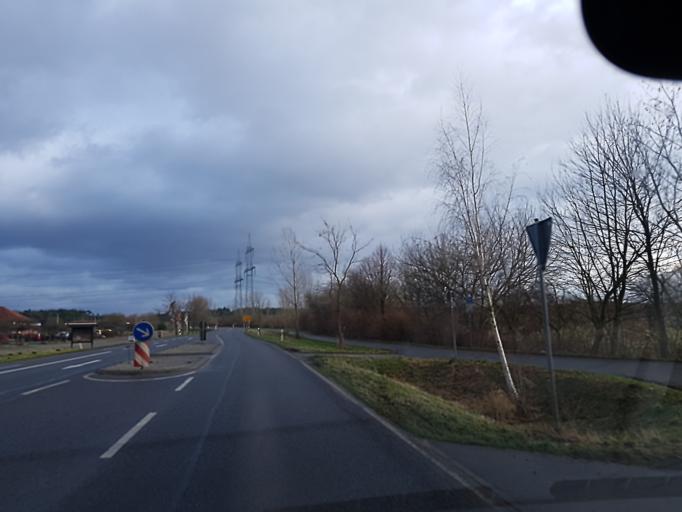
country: DE
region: Brandenburg
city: Bad Liebenwerda
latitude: 51.5145
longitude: 13.4230
